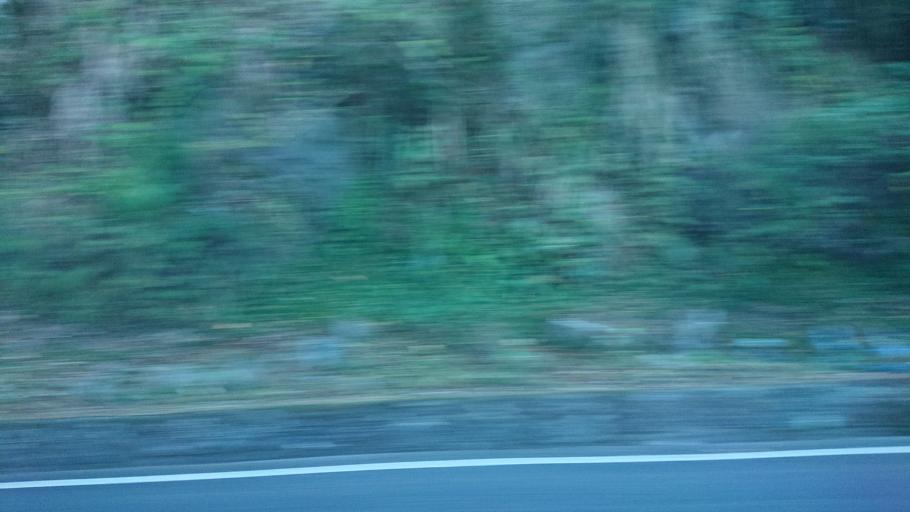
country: TW
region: Taiwan
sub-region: Chiayi
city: Jiayi Shi
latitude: 23.4683
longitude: 120.7184
